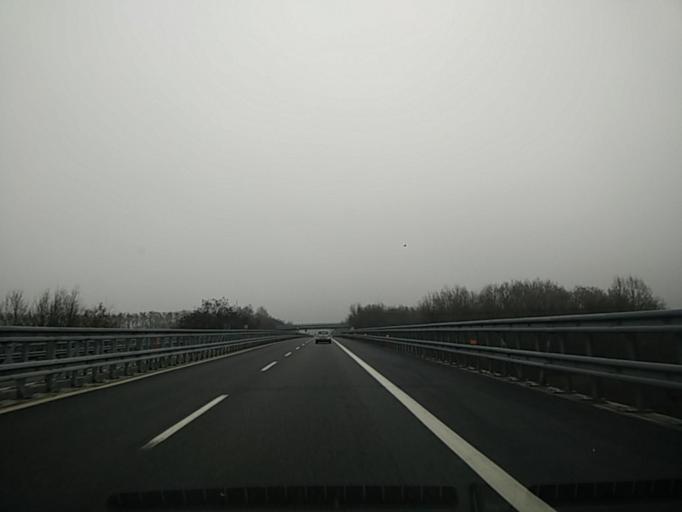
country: IT
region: Piedmont
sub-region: Provincia di Alessandria
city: Quattordio
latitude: 44.9056
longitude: 8.3848
